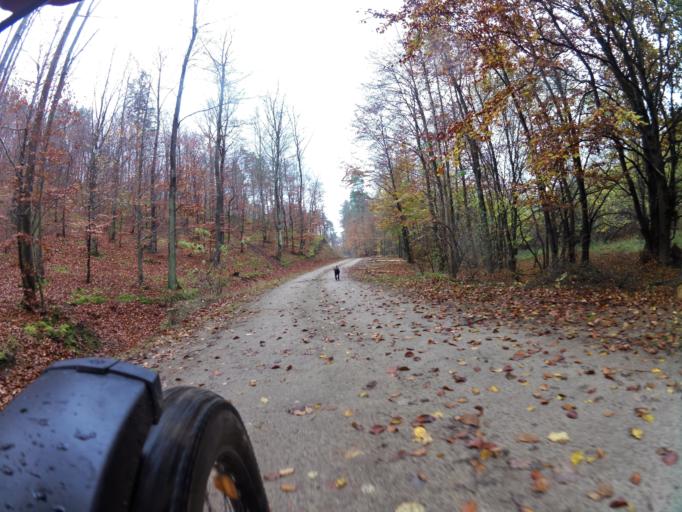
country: PL
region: Pomeranian Voivodeship
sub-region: Powiat pucki
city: Krokowa
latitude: 54.7508
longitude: 18.0916
